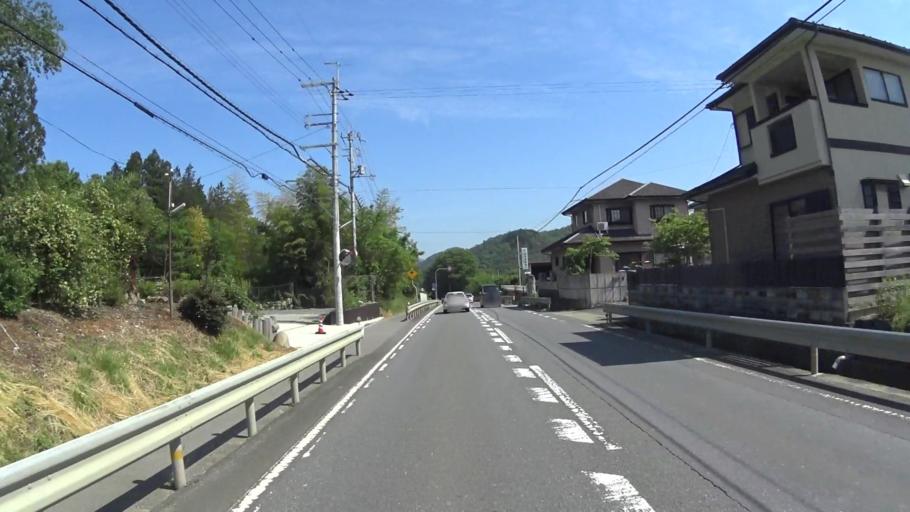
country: JP
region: Kyoto
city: Ayabe
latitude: 35.1711
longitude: 135.4244
